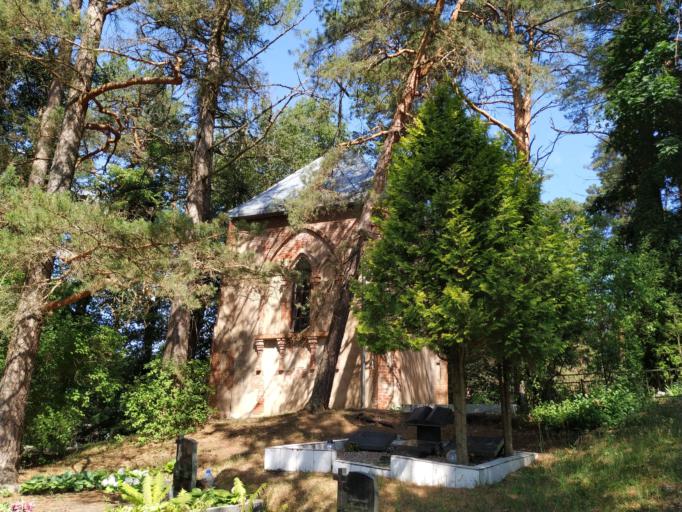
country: LT
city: Nemencine
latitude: 54.7975
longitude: 25.4008
